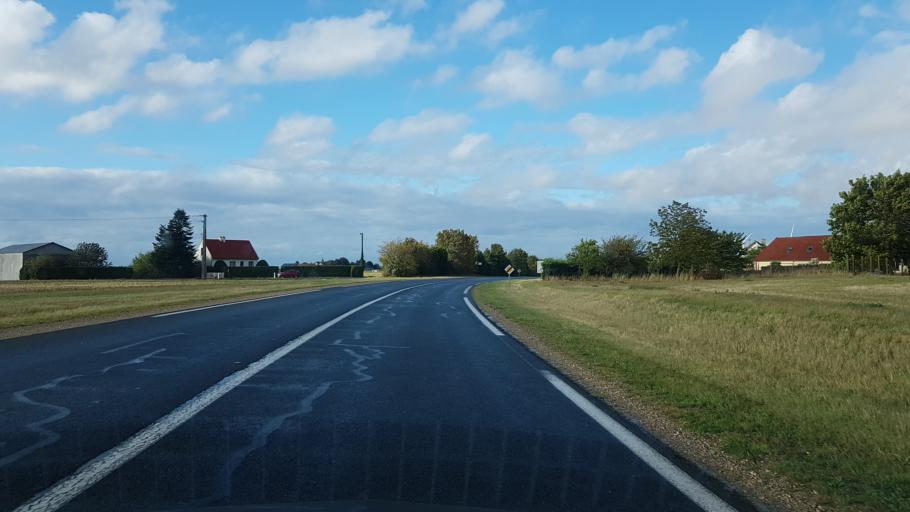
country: FR
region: Centre
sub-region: Departement du Loiret
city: Sermaises
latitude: 48.2593
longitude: 2.2110
